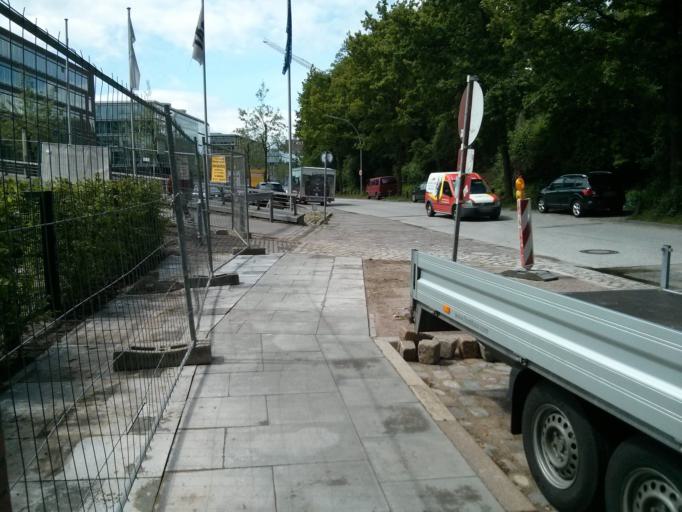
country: DE
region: Hamburg
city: Altona
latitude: 53.5449
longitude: 9.9251
